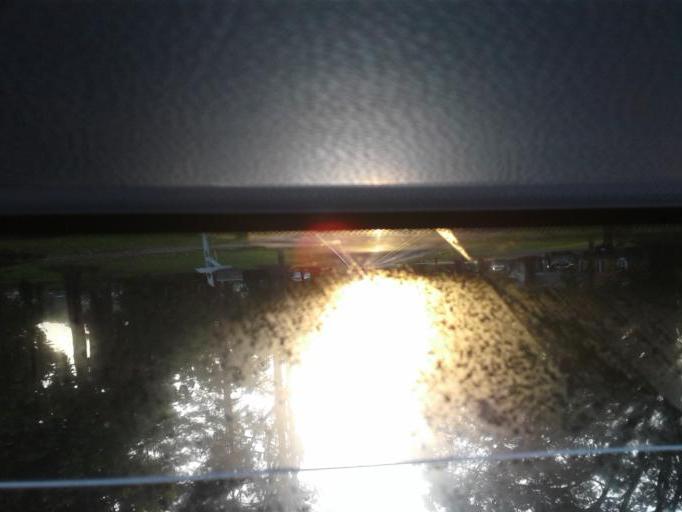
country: US
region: North Carolina
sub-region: Harnett County
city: Erwin
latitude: 35.3223
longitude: -78.6707
